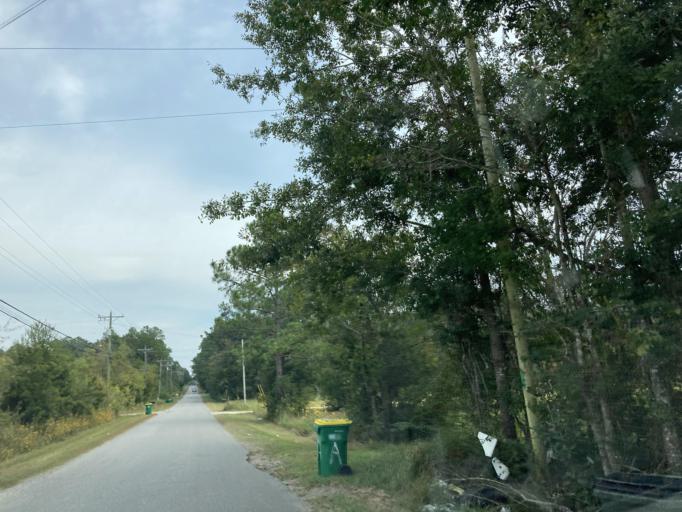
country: US
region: Mississippi
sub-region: Jackson County
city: Saint Martin
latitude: 30.4648
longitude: -88.8602
